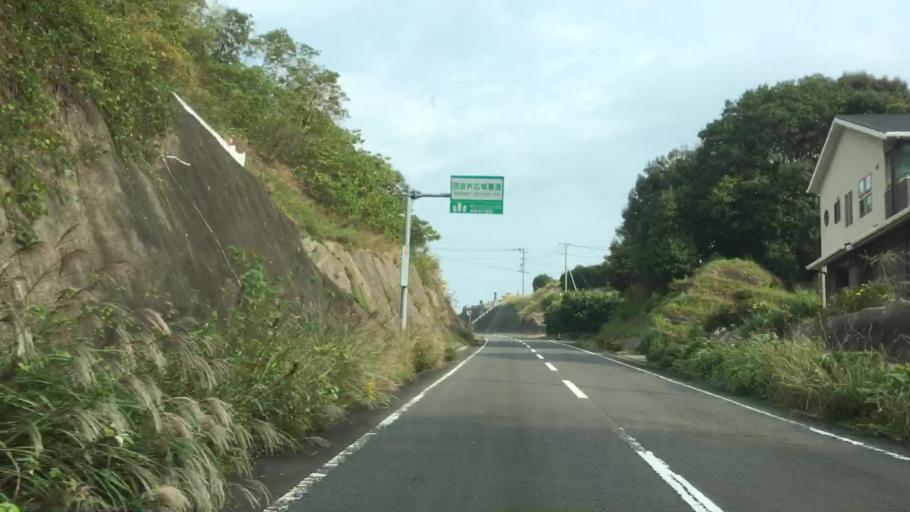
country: JP
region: Nagasaki
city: Sasebo
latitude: 32.9908
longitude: 129.7220
